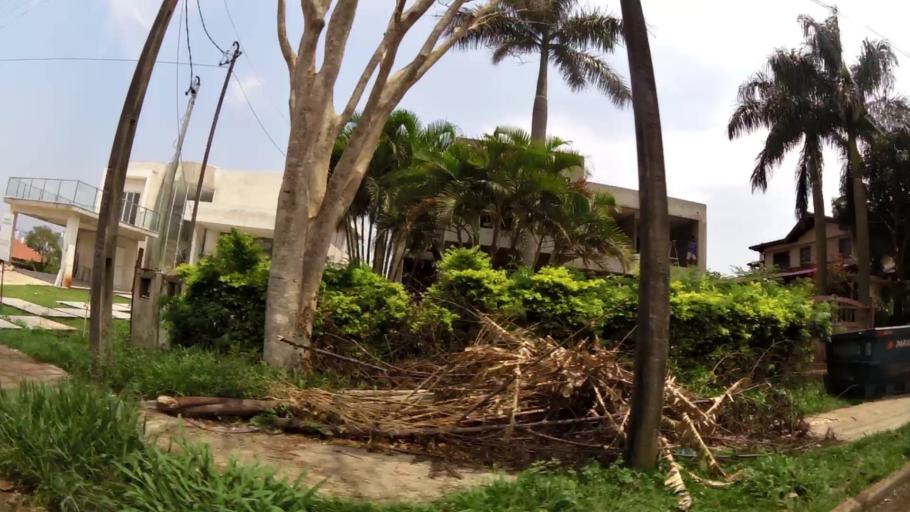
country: PY
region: Alto Parana
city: Ciudad del Este
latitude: -25.4963
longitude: -54.6102
